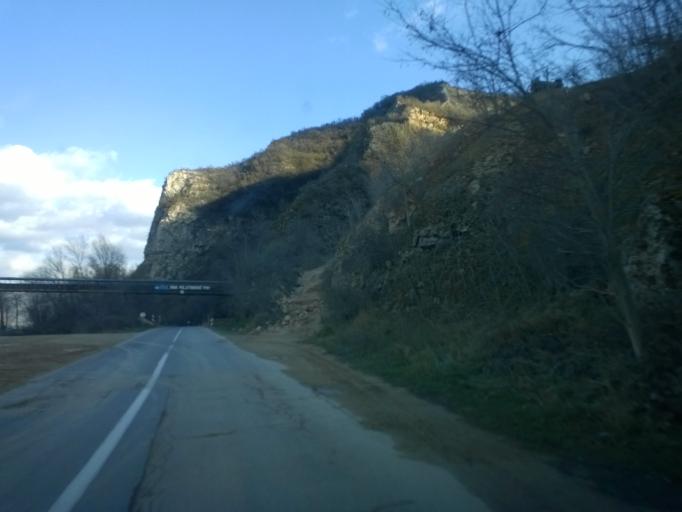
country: RO
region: Caras-Severin
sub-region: Comuna Pescari
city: Coronini
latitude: 44.6520
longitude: 21.7324
